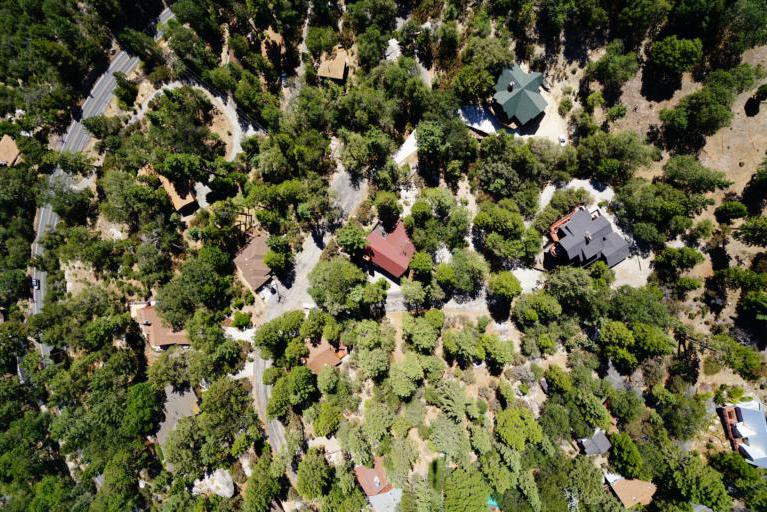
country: US
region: California
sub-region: Riverside County
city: Idyllwild-Pine Cove
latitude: 33.7503
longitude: -116.7368
